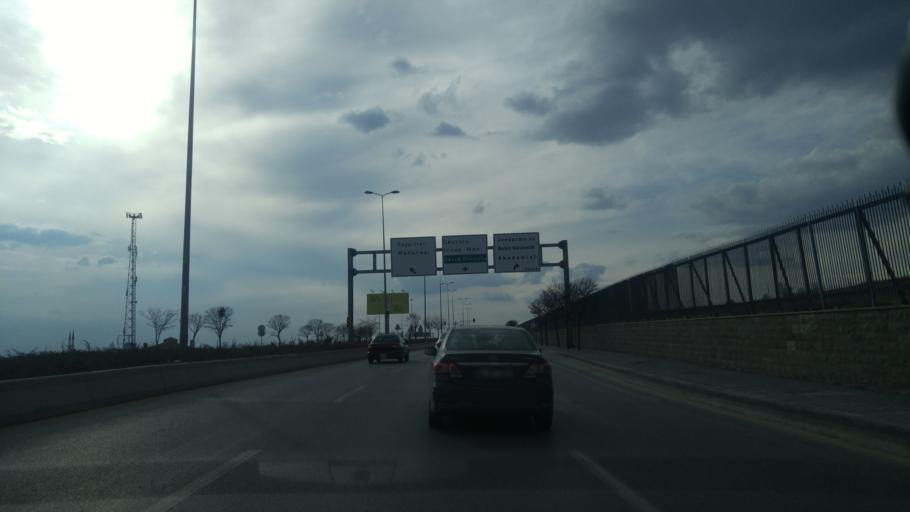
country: TR
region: Ankara
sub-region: Goelbasi
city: Golbasi
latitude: 39.8356
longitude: 32.7675
